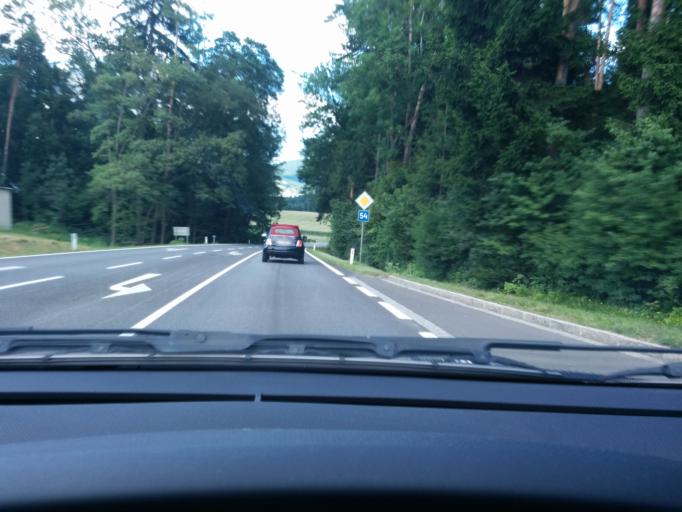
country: AT
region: Styria
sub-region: Politischer Bezirk Hartberg-Fuerstenfeld
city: Hartberg
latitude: 47.2537
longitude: 15.9364
